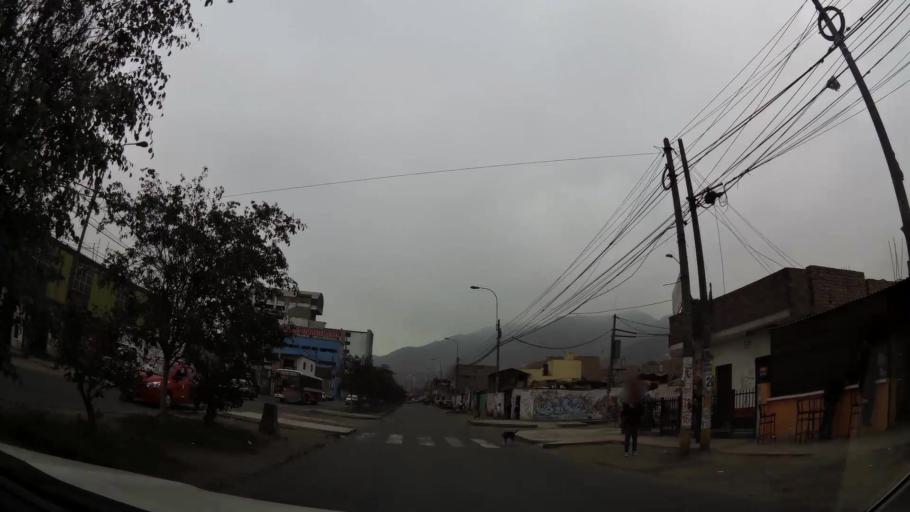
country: PE
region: Lima
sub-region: Lima
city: Independencia
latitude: -11.9791
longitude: -77.0114
